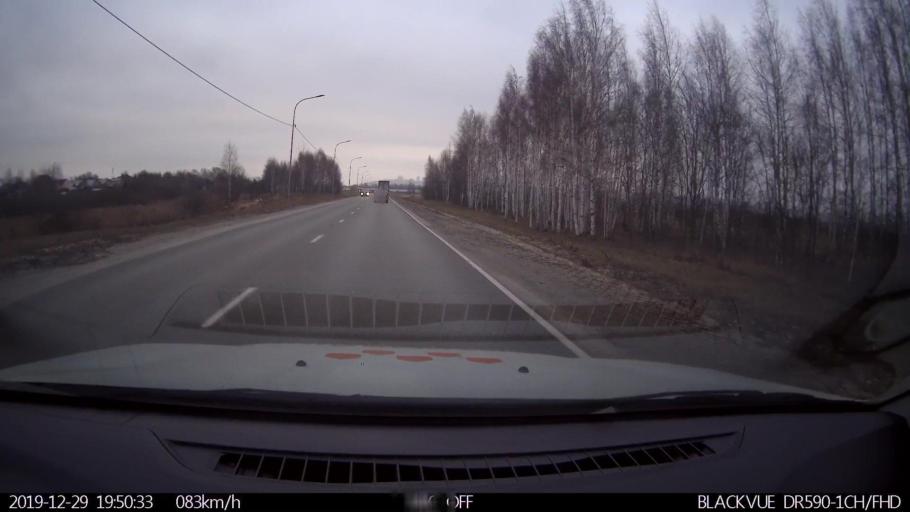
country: RU
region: Nizjnij Novgorod
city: Bor
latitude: 56.3668
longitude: 44.0295
